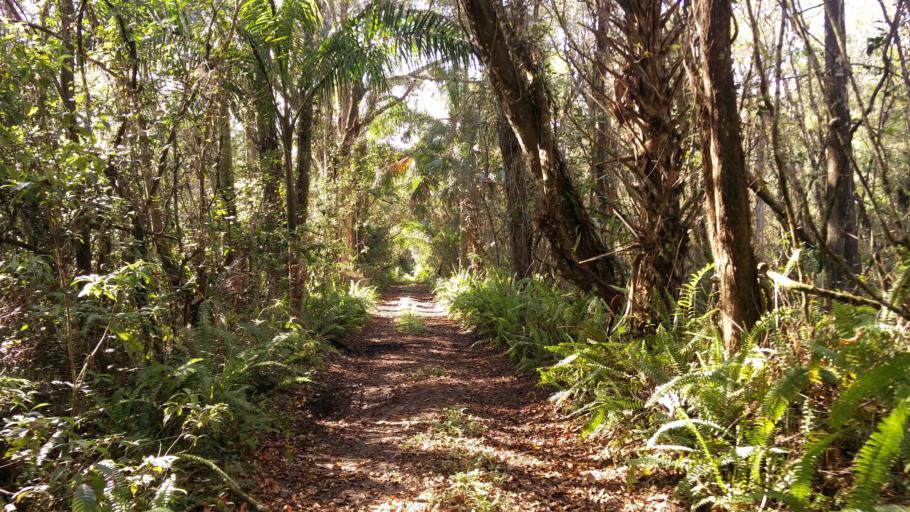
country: US
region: Florida
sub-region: Collier County
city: Lely Resort
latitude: 25.9796
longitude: -81.4225
